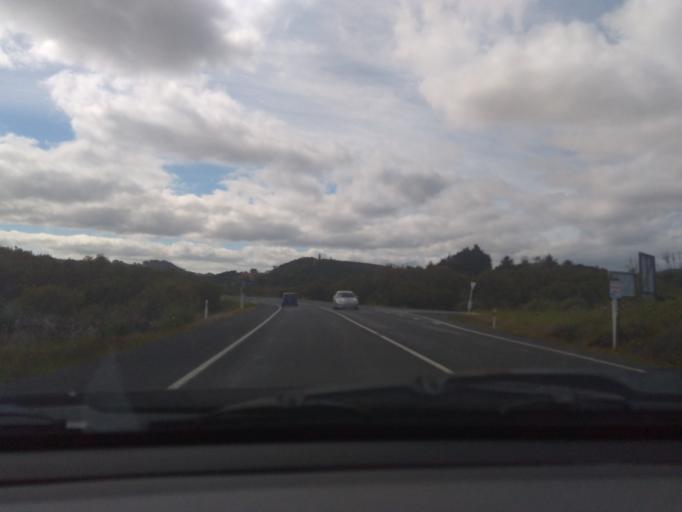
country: NZ
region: Northland
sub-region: Far North District
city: Taipa
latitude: -35.0106
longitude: 173.5425
